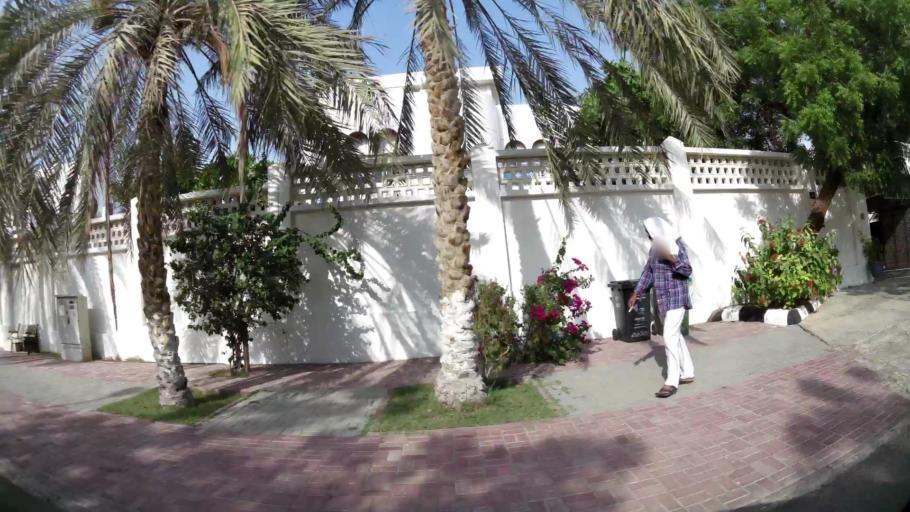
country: AE
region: Ash Shariqah
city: Sharjah
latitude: 25.2478
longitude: 55.4202
